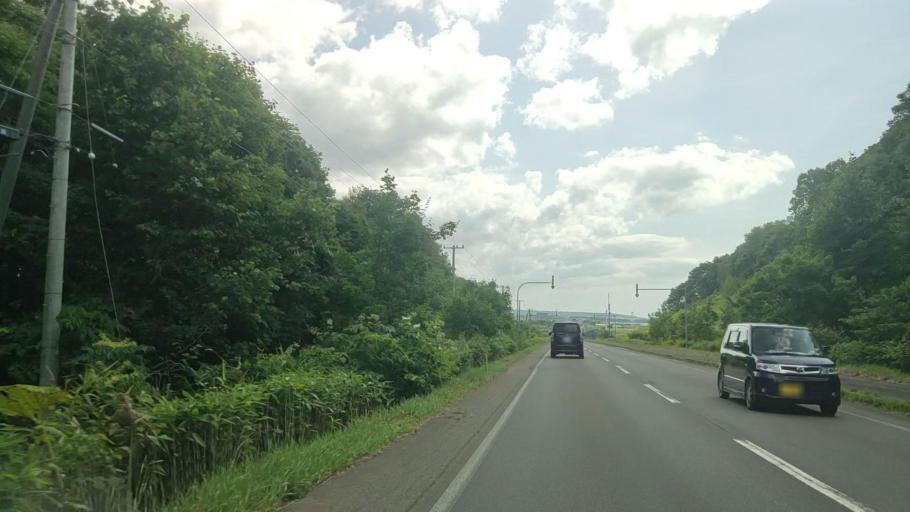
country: JP
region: Hokkaido
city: Makubetsu
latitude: 44.7632
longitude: 141.7937
